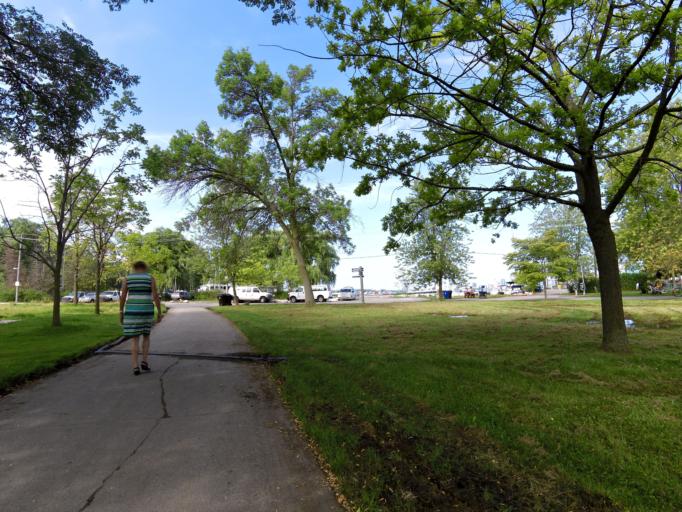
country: CA
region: Ontario
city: Toronto
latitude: 43.6310
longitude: -79.3564
